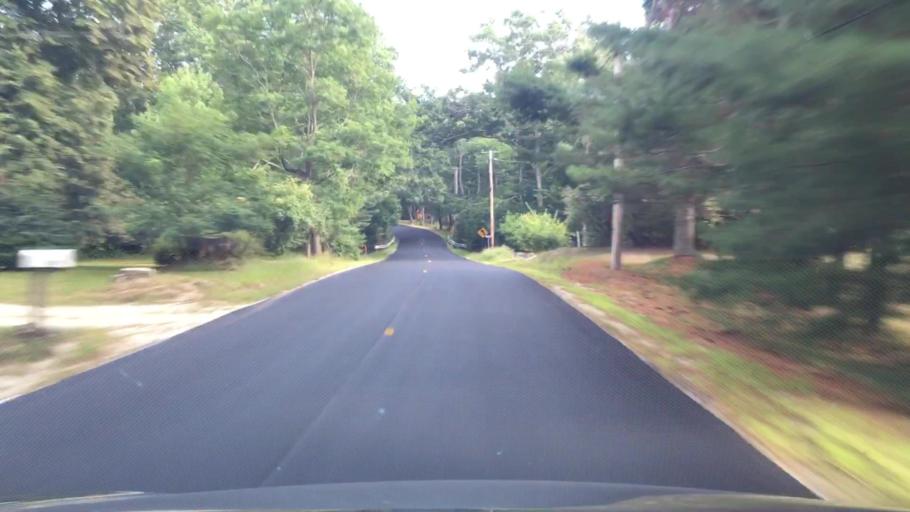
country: US
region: Maine
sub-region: Hancock County
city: Surry
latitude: 44.5186
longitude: -68.6074
